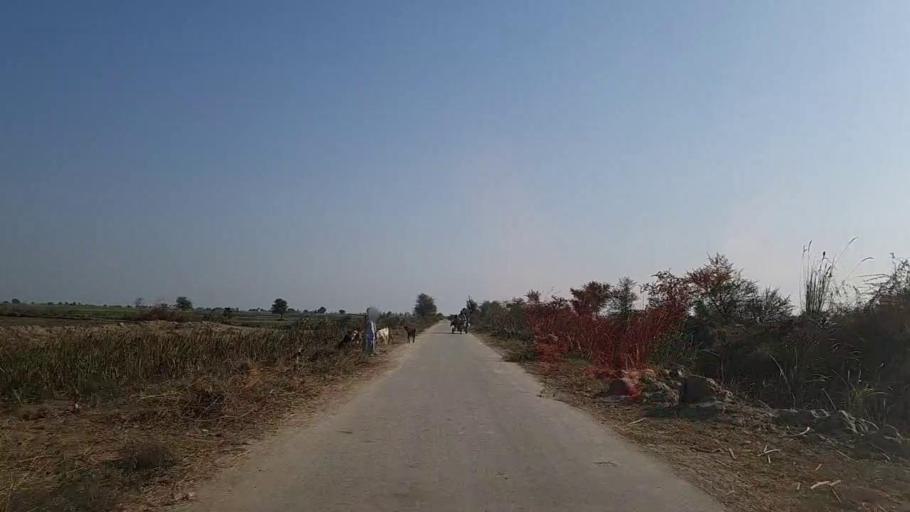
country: PK
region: Sindh
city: Sanghar
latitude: 25.9482
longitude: 69.0489
